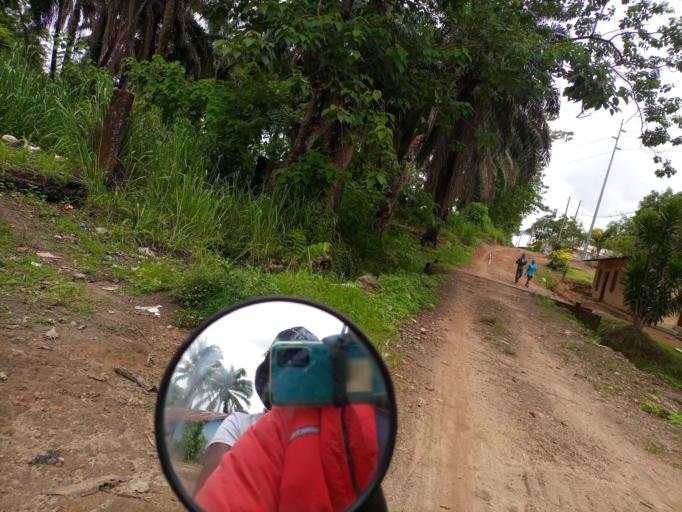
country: SL
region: Southern Province
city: Bo
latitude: 7.9557
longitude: -11.7446
